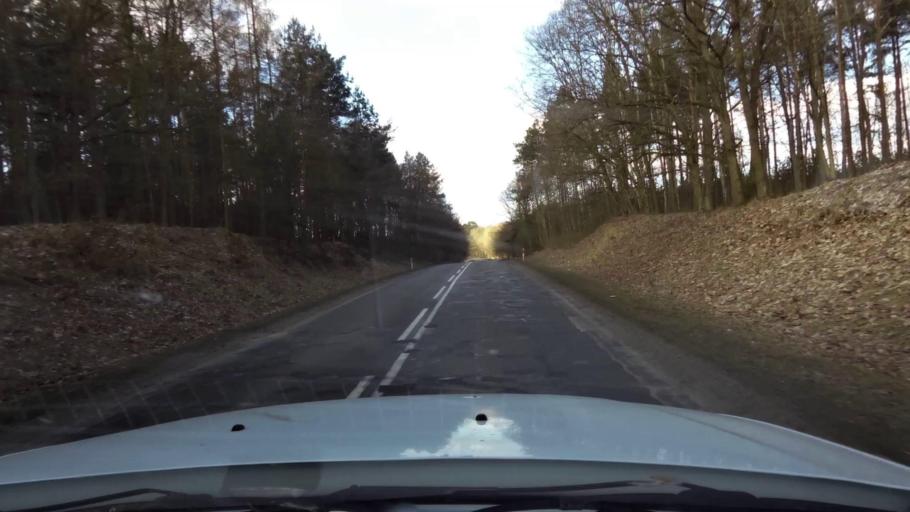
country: PL
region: West Pomeranian Voivodeship
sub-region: Powiat choszczenski
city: Pelczyce
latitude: 53.0667
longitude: 15.2983
